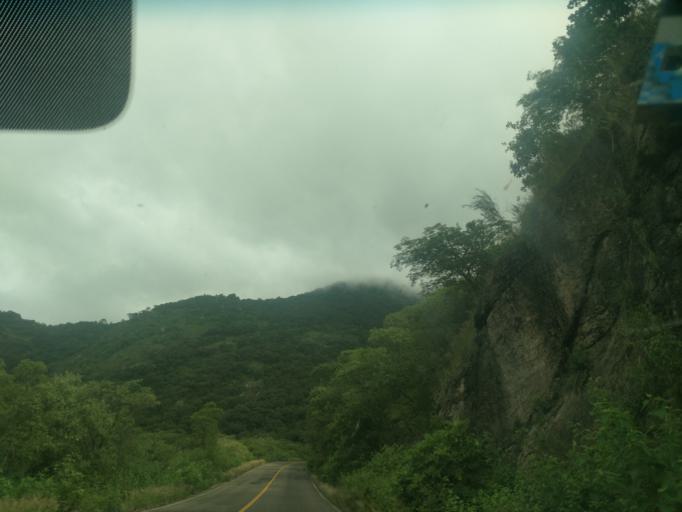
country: MX
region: Jalisco
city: El Salto
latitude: 20.3652
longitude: -104.5805
